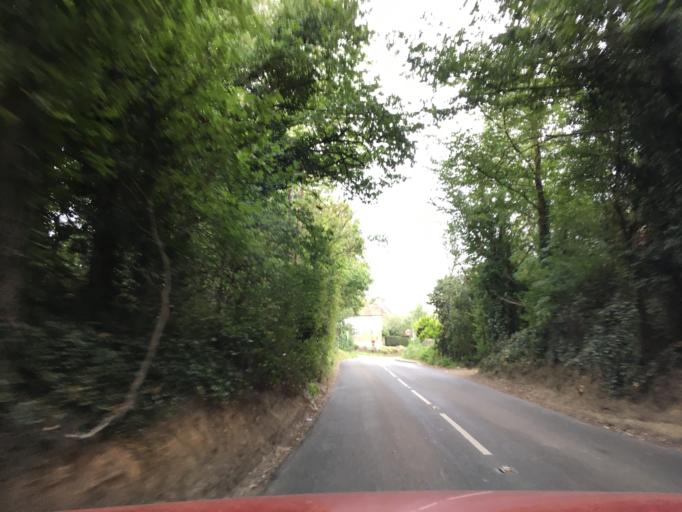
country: GB
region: England
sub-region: Kent
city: Yalding
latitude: 51.2294
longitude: 0.4342
